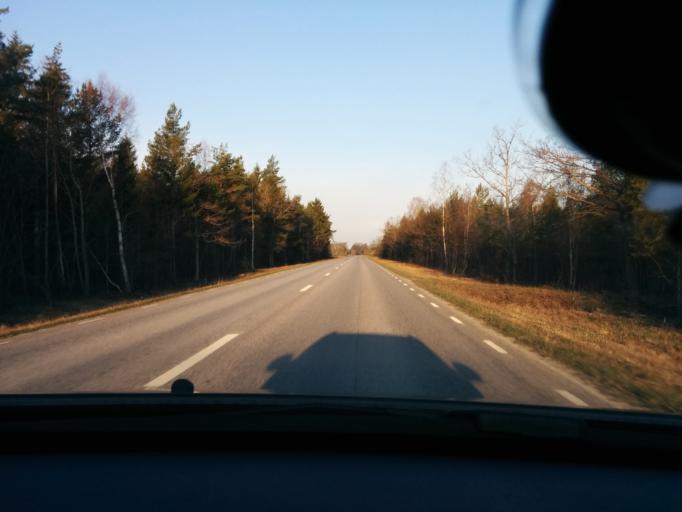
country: SE
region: Gotland
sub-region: Gotland
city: Visby
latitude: 57.6397
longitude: 18.4924
